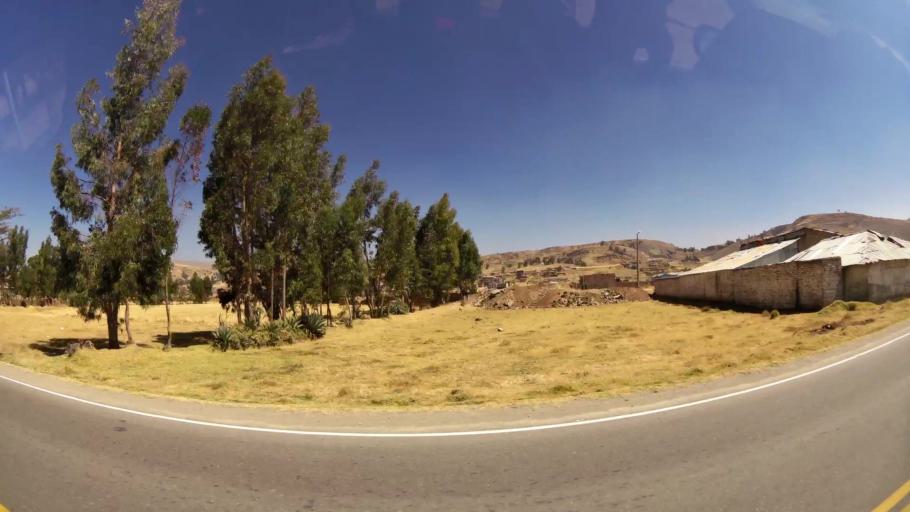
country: PE
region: Junin
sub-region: Provincia de Jauja
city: Jauja
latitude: -11.7636
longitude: -75.4954
